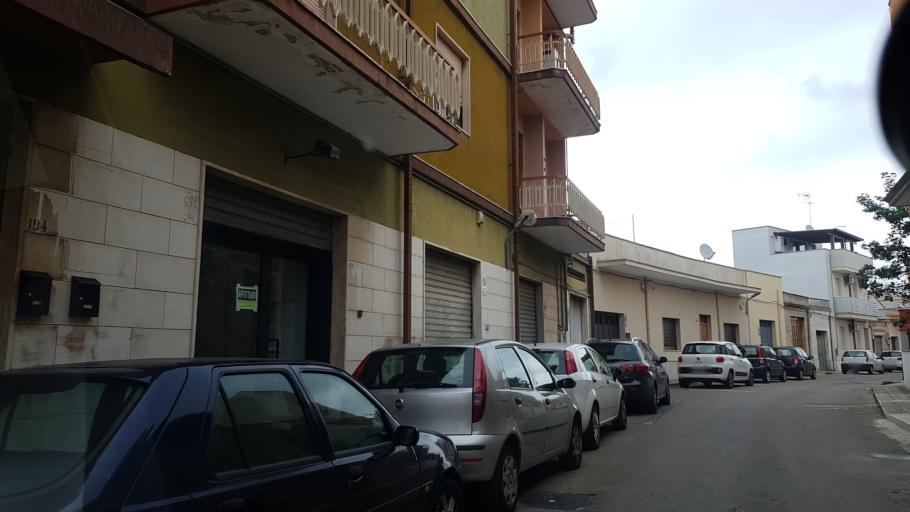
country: IT
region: Apulia
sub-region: Provincia di Brindisi
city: Mesagne
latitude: 40.5635
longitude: 17.8050
